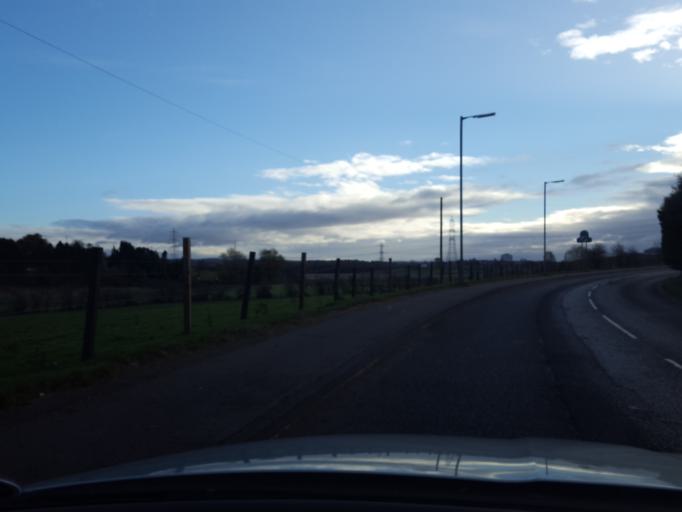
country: GB
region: Scotland
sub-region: North Lanarkshire
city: Glenboig
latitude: 55.8839
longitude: -4.0787
